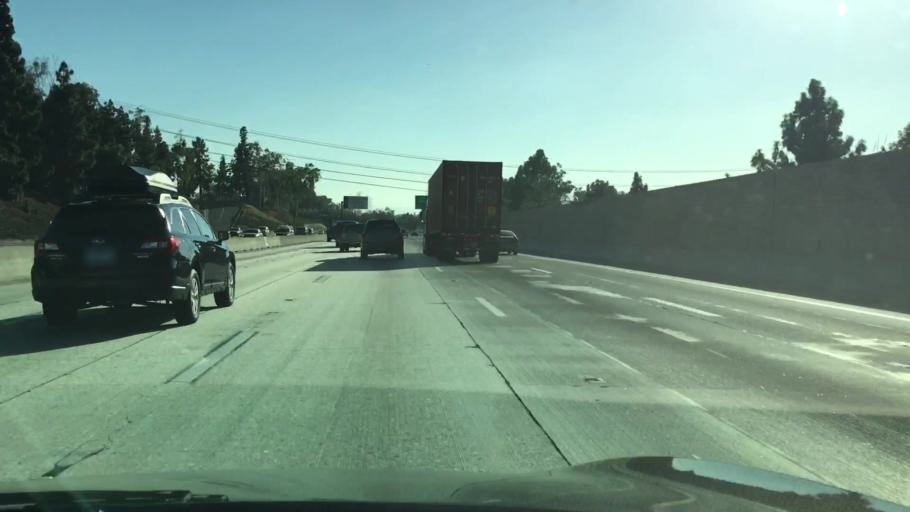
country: US
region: California
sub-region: Los Angeles County
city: West Whittier-Los Nietos
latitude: 34.0074
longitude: -118.0603
